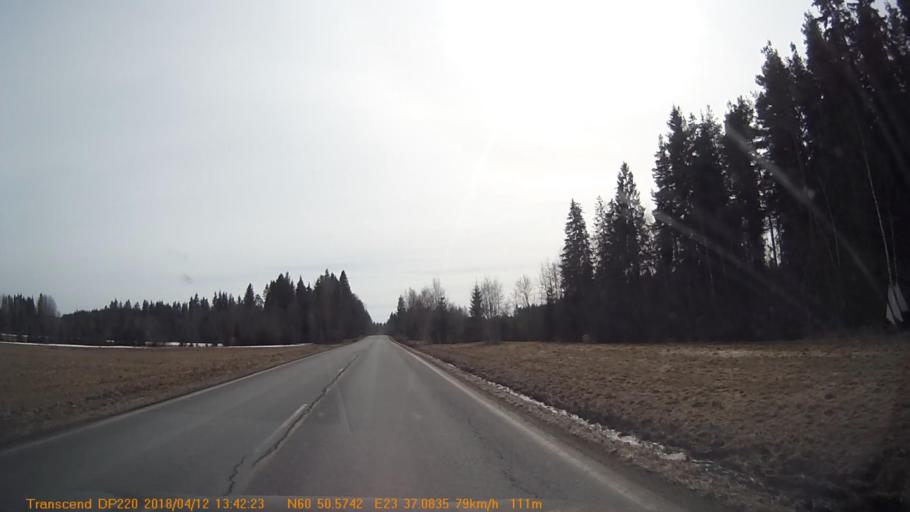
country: FI
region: Haeme
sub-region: Forssa
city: Forssa
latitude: 60.8421
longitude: 23.6181
